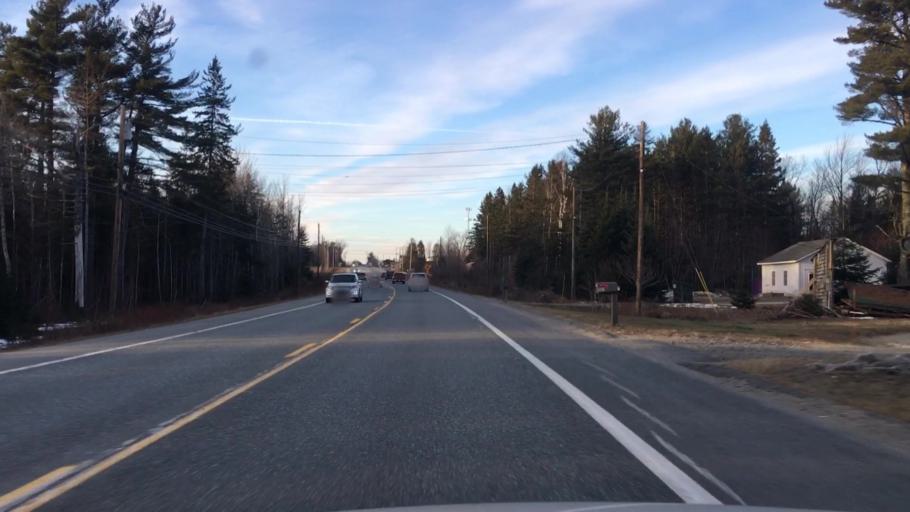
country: US
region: Maine
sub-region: Hancock County
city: Surry
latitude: 44.6124
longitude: -68.5219
